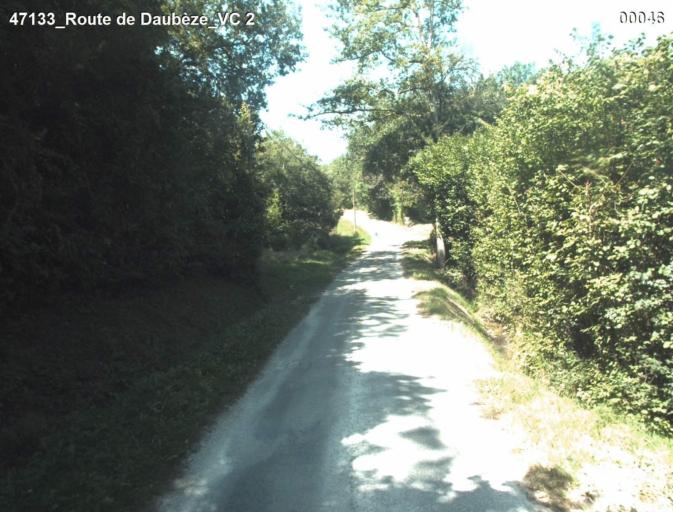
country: FR
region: Aquitaine
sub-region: Departement du Lot-et-Garonne
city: Laplume
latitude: 44.0848
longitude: 0.5340
